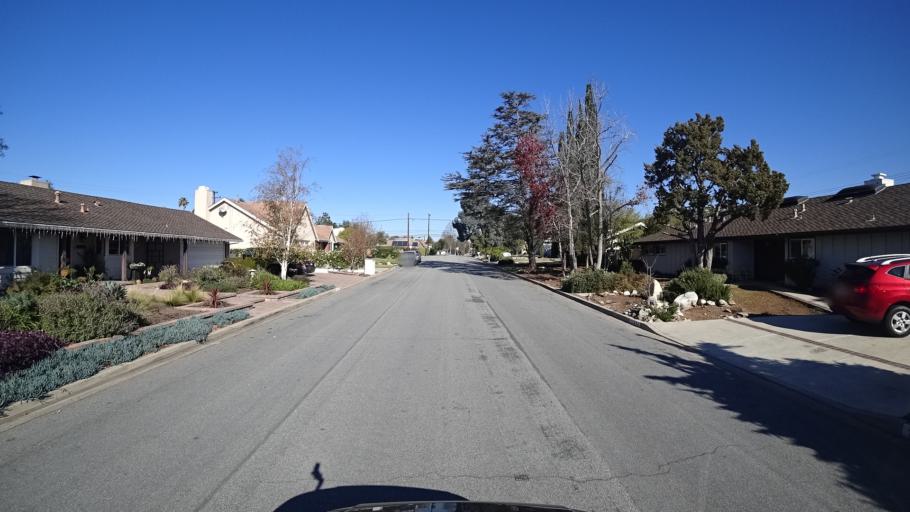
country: US
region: California
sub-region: Orange County
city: North Tustin
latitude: 33.7725
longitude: -117.8080
